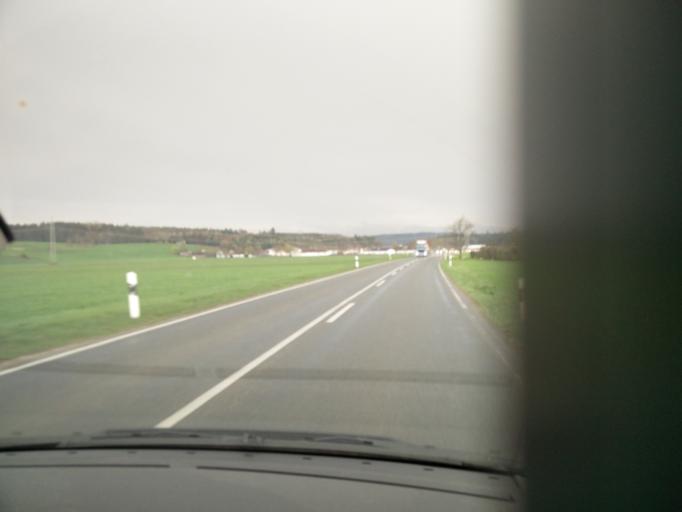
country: DE
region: Bavaria
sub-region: Upper Bavaria
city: Bad Endorf
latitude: 47.9246
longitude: 12.2907
